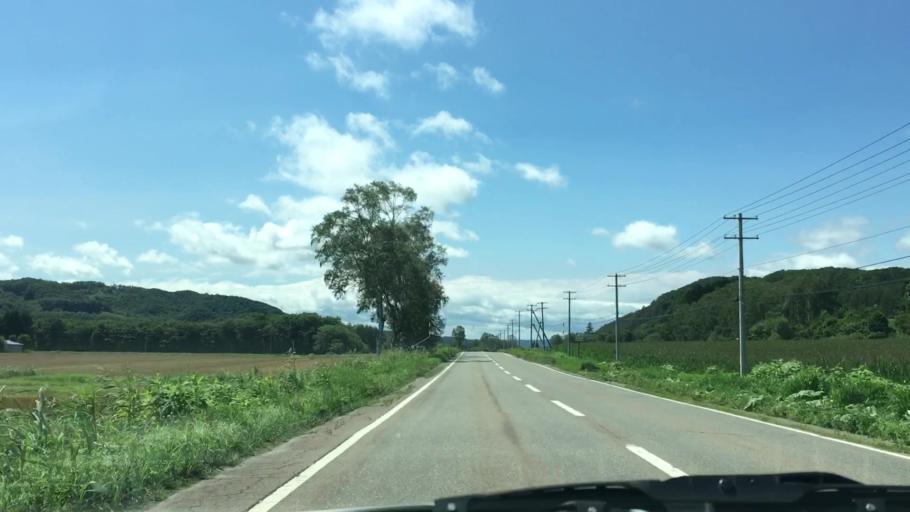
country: JP
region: Hokkaido
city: Kitami
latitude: 43.2983
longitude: 143.6780
